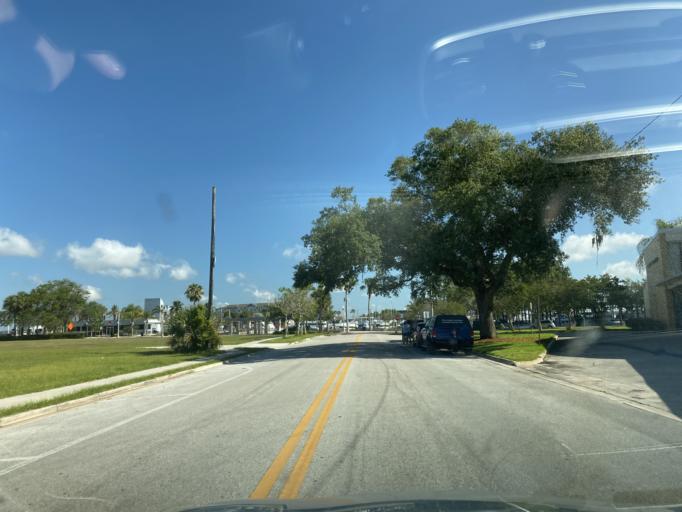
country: US
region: Florida
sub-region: Seminole County
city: Sanford
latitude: 28.8127
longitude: -81.2649
